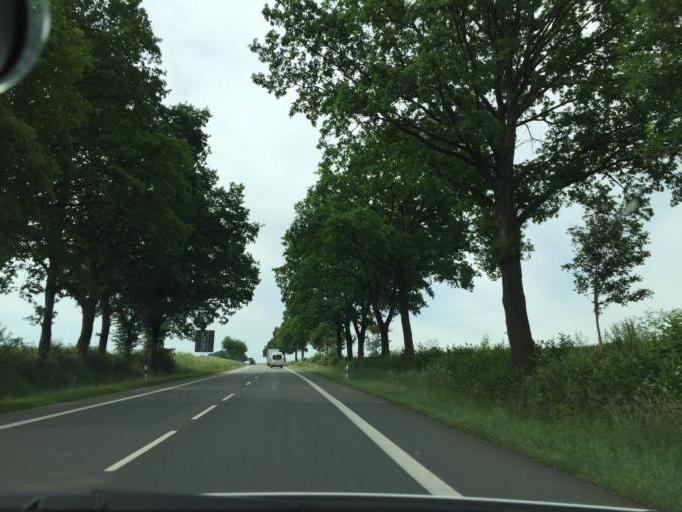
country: DE
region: North Rhine-Westphalia
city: Warburg
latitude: 51.5497
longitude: 9.1322
